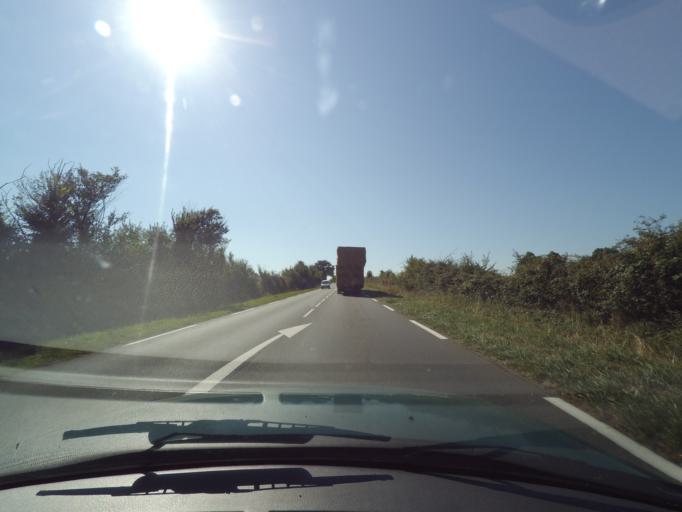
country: FR
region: Poitou-Charentes
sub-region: Departement de la Vienne
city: Lussac-les-Chateaux
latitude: 46.3889
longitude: 0.7411
